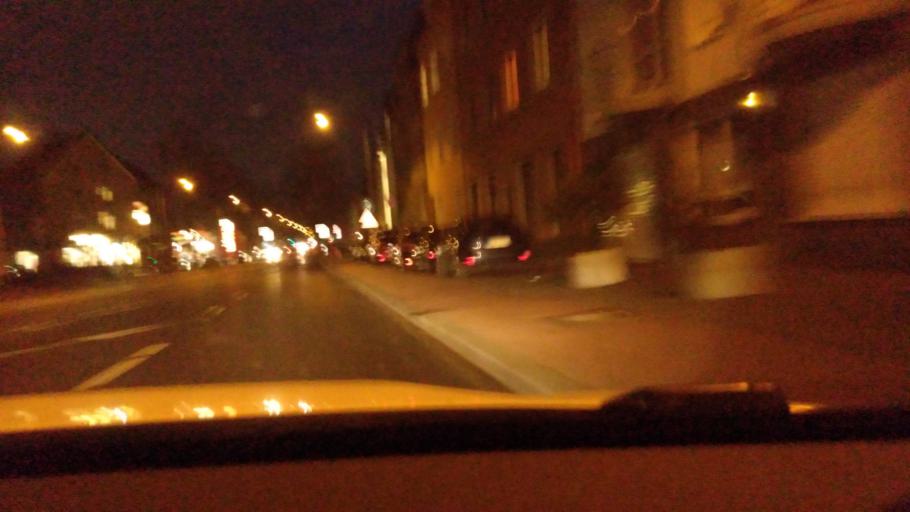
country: DE
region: North Rhine-Westphalia
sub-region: Regierungsbezirk Koln
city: Bayenthal
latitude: 50.8974
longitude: 6.9513
